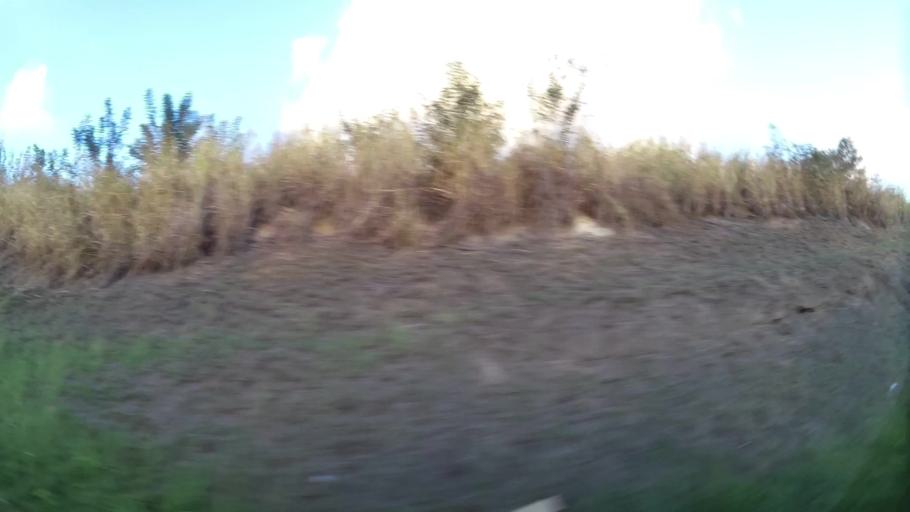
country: KN
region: Saint Anne Sandy Point
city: Sandy Point Town
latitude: 17.3699
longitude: -62.8520
